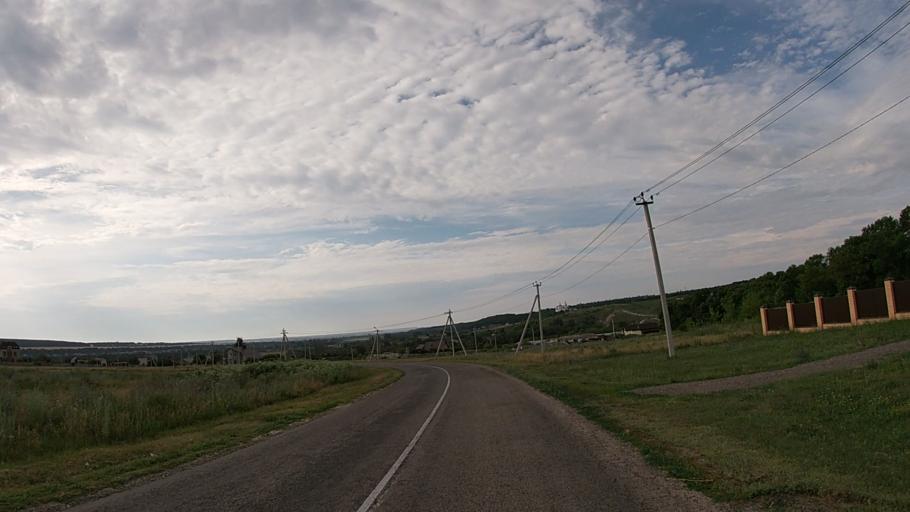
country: RU
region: Belgorod
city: Severnyy
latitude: 50.7155
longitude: 36.5910
